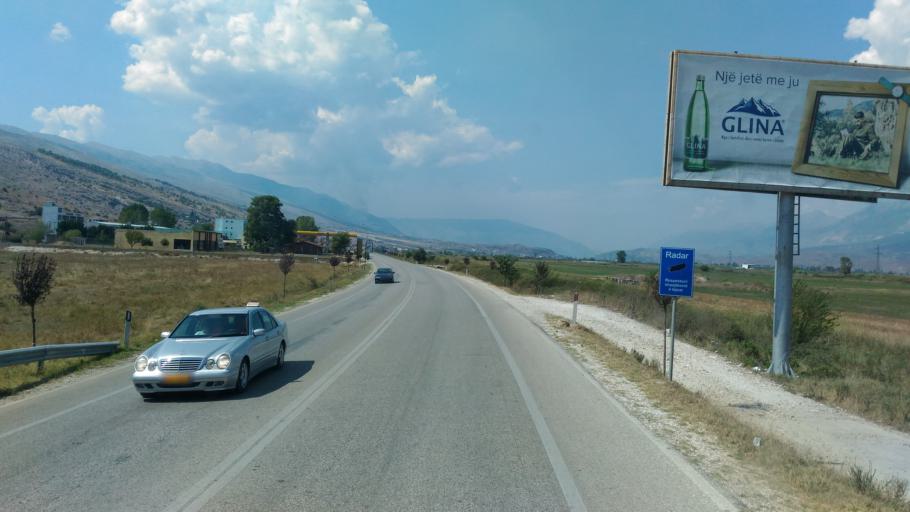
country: AL
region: Gjirokaster
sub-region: Rrethi i Gjirokastres
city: Dervician
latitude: 40.0053
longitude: 20.2094
